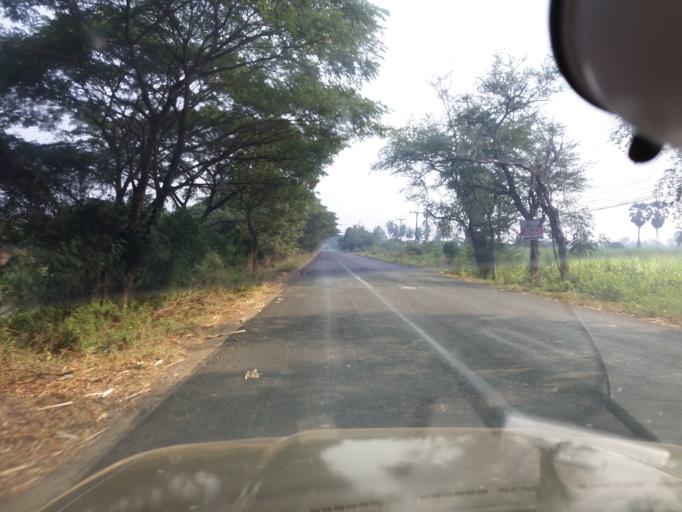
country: TH
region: Sing Buri
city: Bang Racham
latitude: 14.9181
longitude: 100.2576
